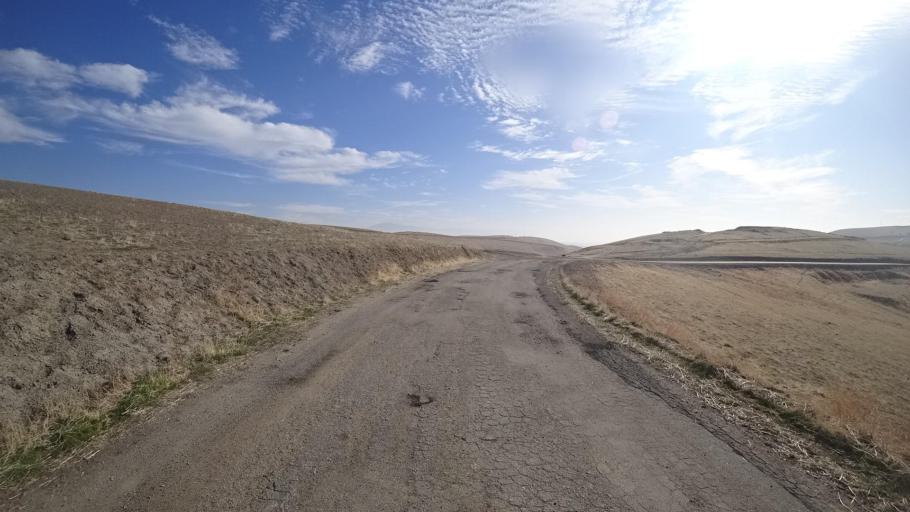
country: US
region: California
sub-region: Kern County
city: Oildale
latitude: 35.4875
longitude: -118.8799
